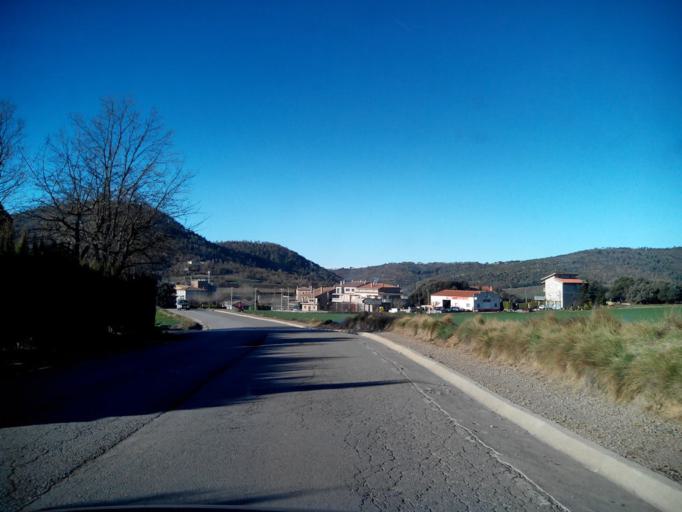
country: ES
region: Catalonia
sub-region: Provincia de Barcelona
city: Capolat
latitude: 42.0212
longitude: 1.7393
